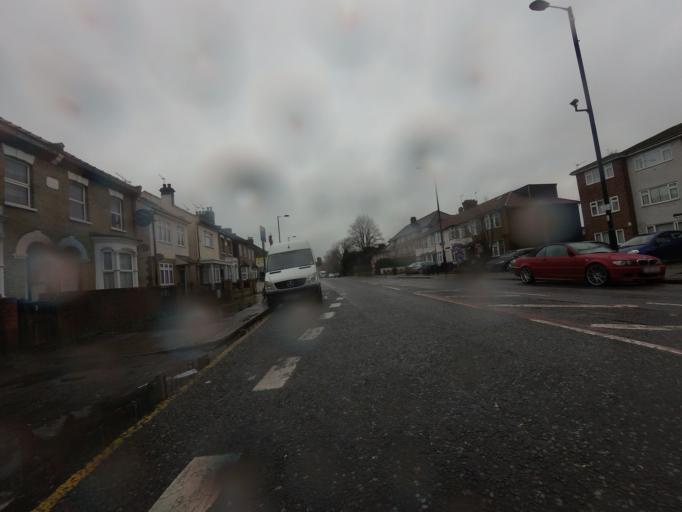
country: GB
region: England
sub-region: Hertfordshire
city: Waltham Cross
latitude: 51.6772
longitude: -0.0350
